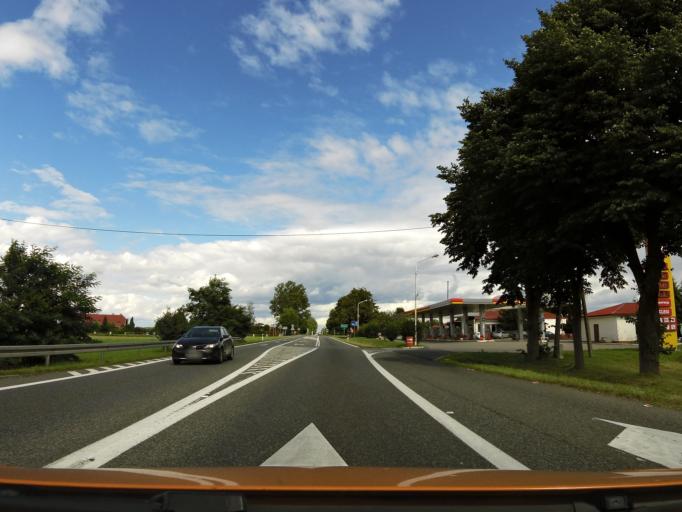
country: PL
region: West Pomeranian Voivodeship
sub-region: Powiat goleniowski
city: Osina
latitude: 53.6419
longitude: 15.0520
